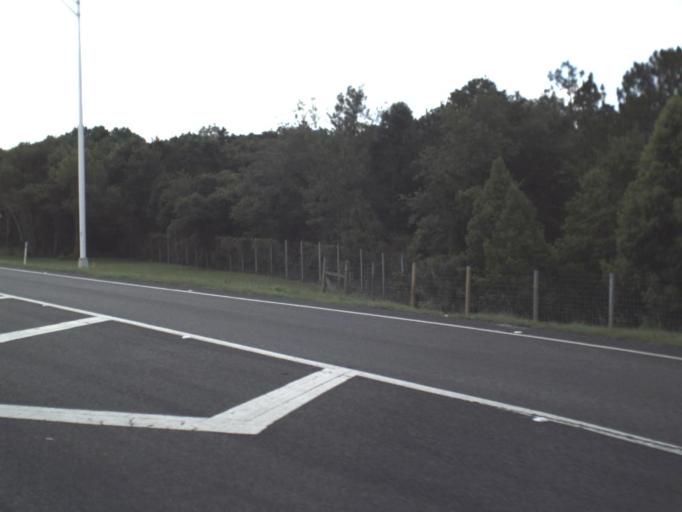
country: US
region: Florida
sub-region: Flagler County
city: Palm Coast
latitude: 29.6644
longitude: -81.2914
